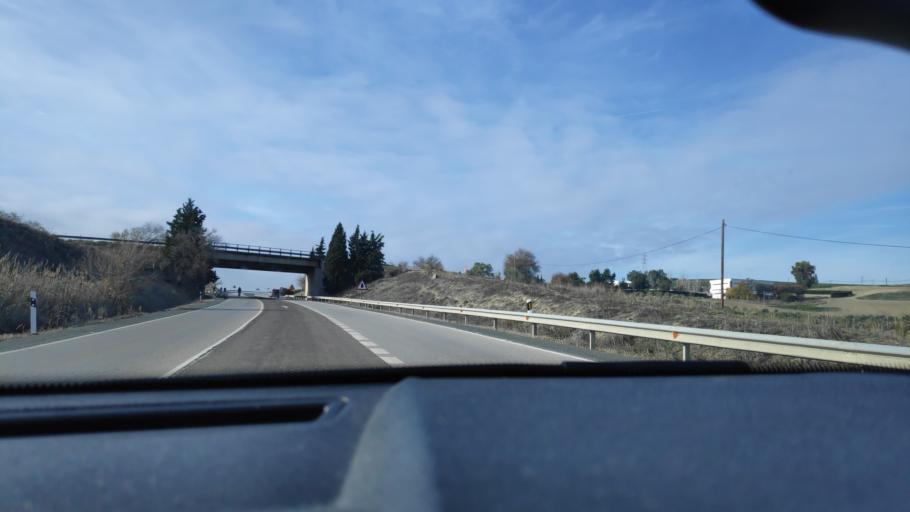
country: ES
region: Andalusia
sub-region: Provincia de Jaen
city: Linares
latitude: 38.0790
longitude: -3.6067
